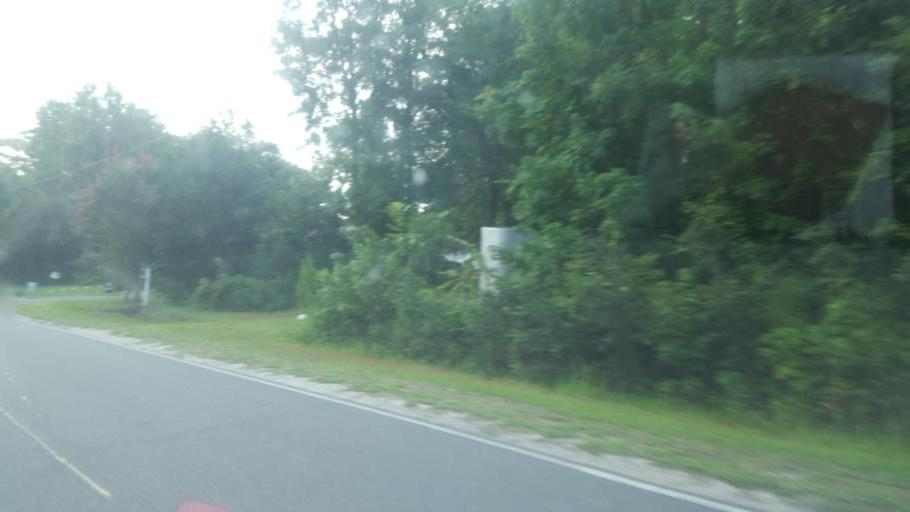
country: US
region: North Carolina
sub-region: Dare County
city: Wanchese
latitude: 35.8419
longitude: -75.6505
